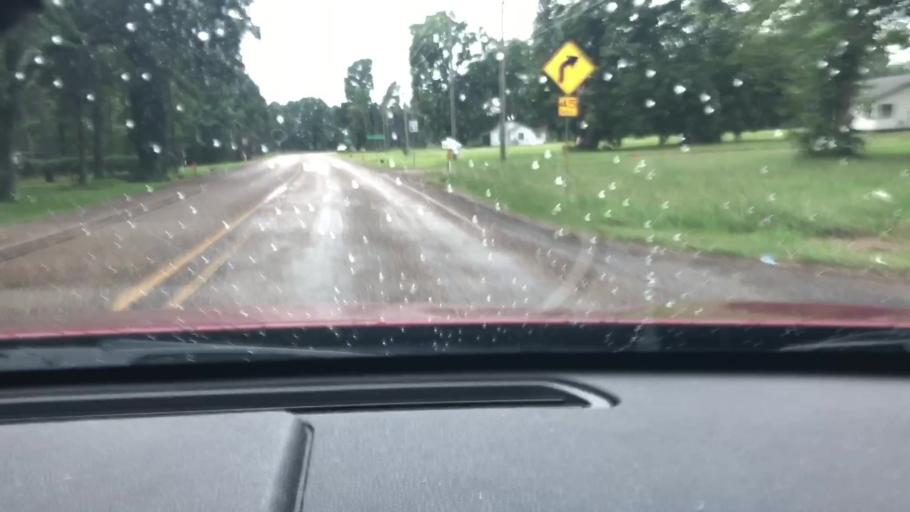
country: US
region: Texas
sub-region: Bowie County
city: Nash
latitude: 33.4424
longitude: -94.1339
